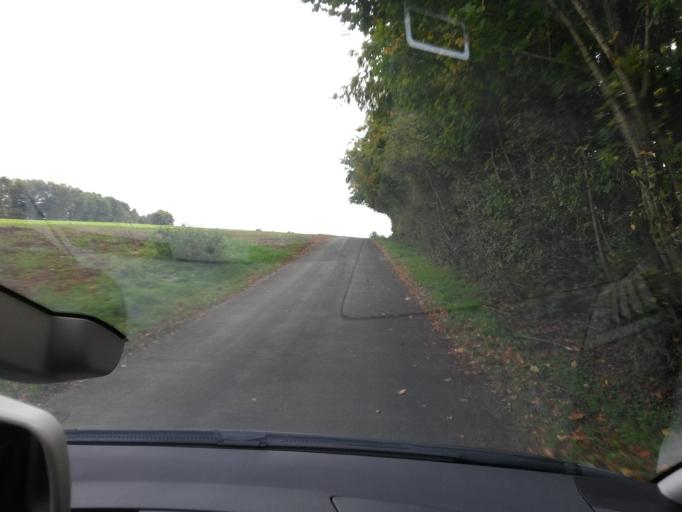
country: BE
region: Wallonia
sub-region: Province du Luxembourg
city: Arlon
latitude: 49.7087
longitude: 5.7877
